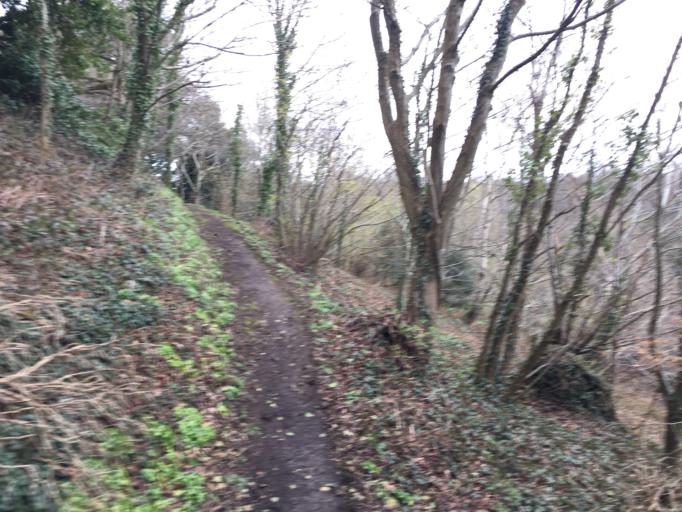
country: JE
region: St Helier
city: Saint Helier
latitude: 49.2161
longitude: -2.1344
